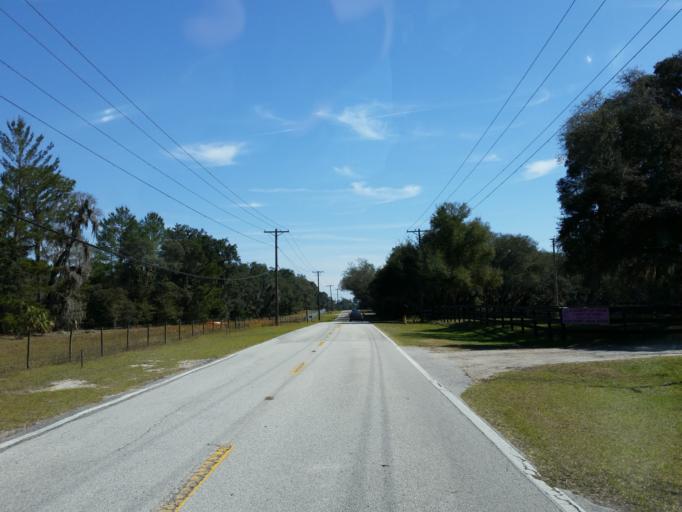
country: US
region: Florida
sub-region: Hillsborough County
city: Boyette
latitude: 27.8355
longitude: -82.2544
